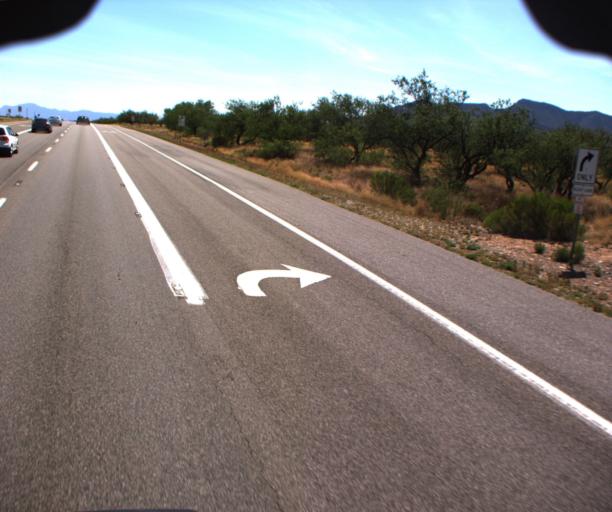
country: US
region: Arizona
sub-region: Cochise County
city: Whetstone
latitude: 31.8373
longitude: -110.3434
